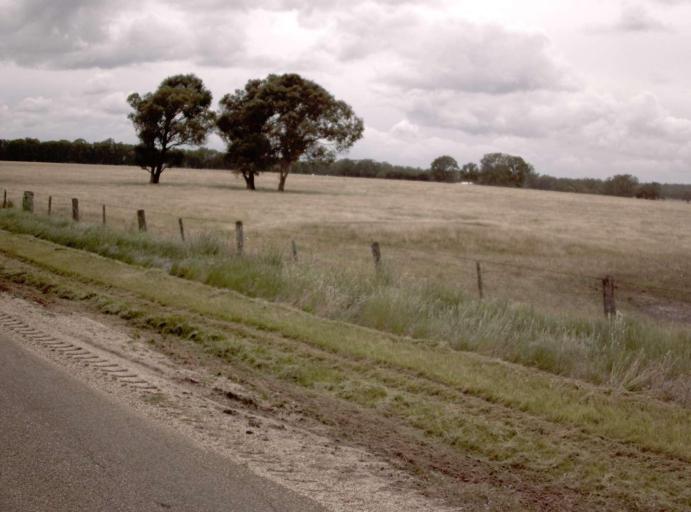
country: AU
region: Victoria
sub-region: Wellington
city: Sale
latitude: -37.8771
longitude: 147.0660
